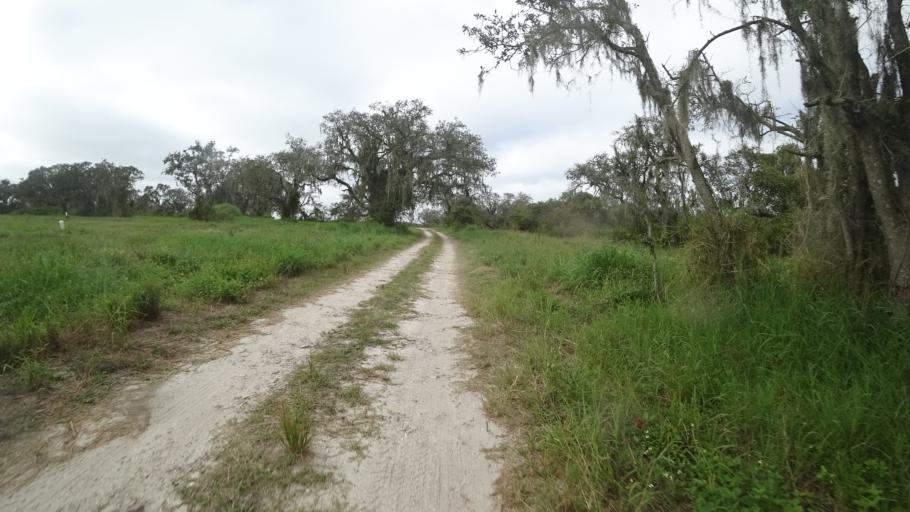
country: US
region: Florida
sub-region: Sarasota County
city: Warm Mineral Springs
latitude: 27.3244
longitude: -82.1368
